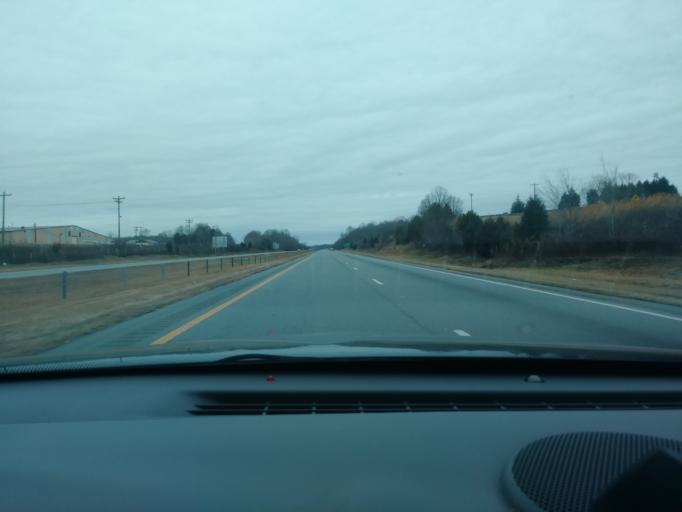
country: US
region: North Carolina
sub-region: Yadkin County
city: Yadkinville
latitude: 36.1195
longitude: -80.6767
